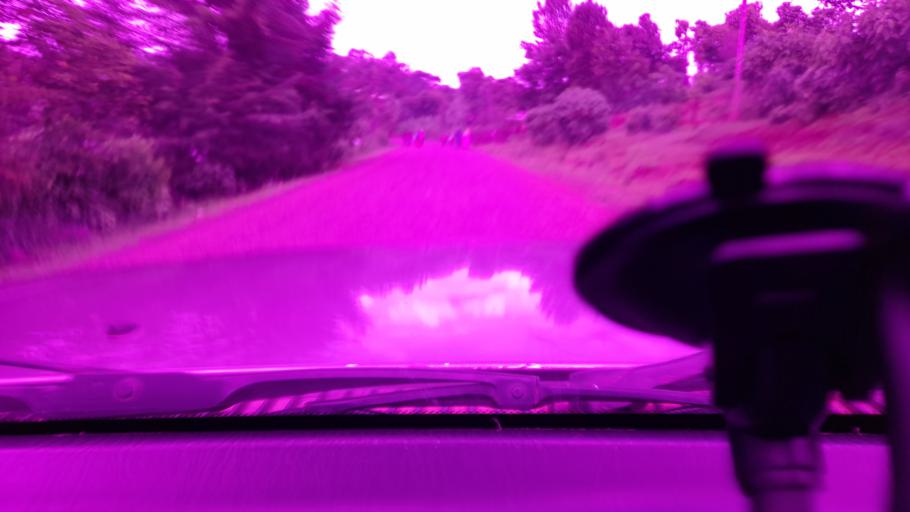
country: ET
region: Oromiya
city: Jima
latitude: 7.9886
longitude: 37.4838
